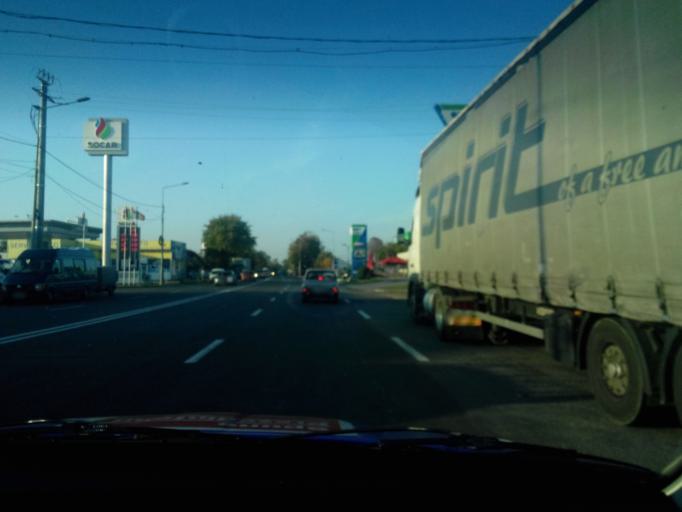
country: RO
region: Vrancea
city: Adjud
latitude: 46.0890
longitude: 27.1902
